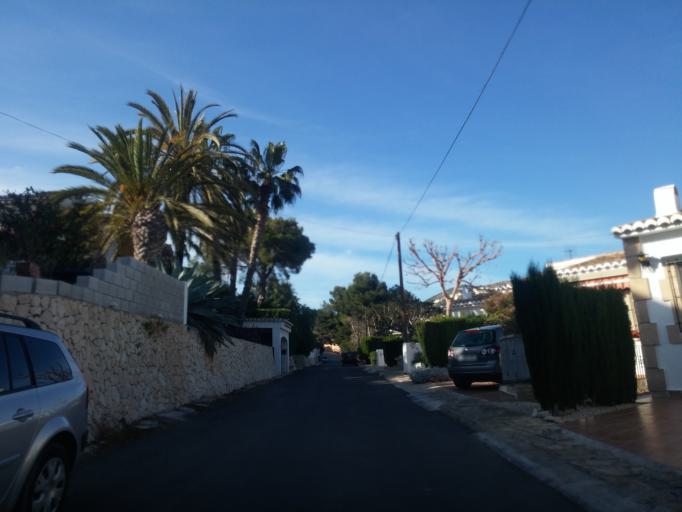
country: ES
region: Valencia
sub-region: Provincia de Alicante
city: Moraira
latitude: 38.6967
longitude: 0.1437
